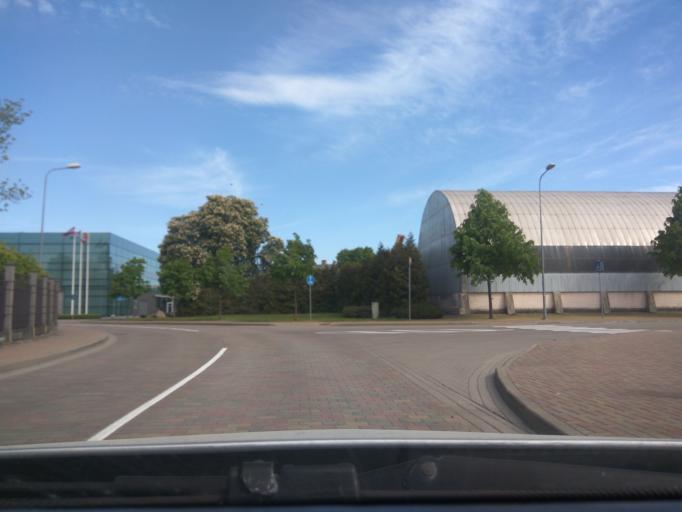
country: LV
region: Ventspils
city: Ventspils
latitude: 57.3976
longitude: 21.5707
